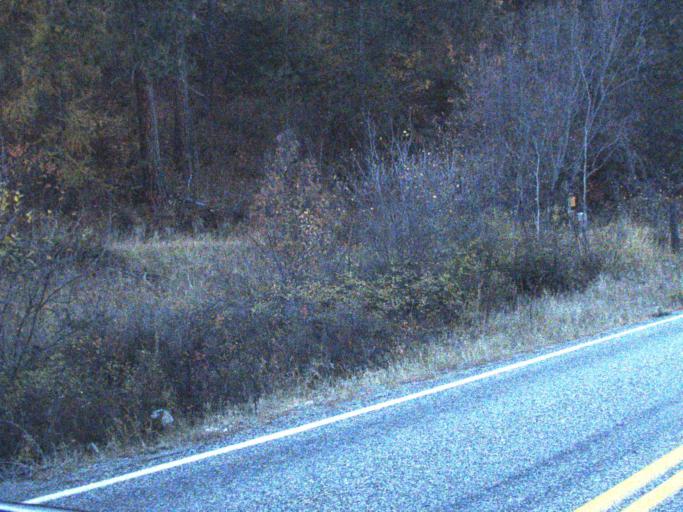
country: CA
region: British Columbia
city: Rossland
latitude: 48.8724
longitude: -117.8467
